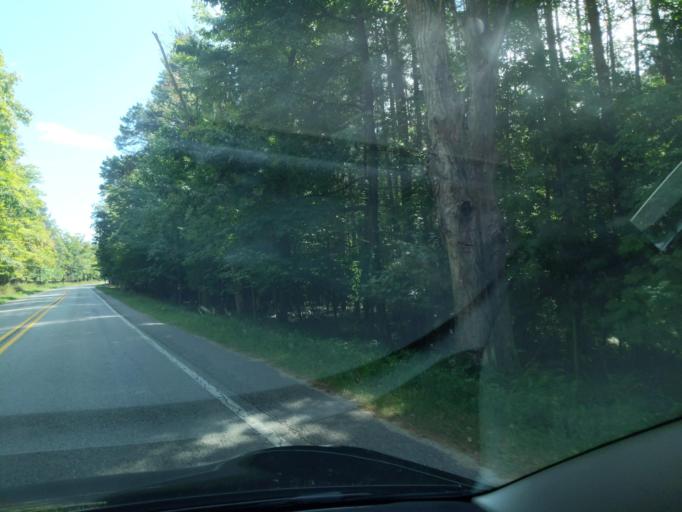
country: US
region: Michigan
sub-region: Antrim County
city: Bellaire
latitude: 45.0697
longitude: -85.3180
